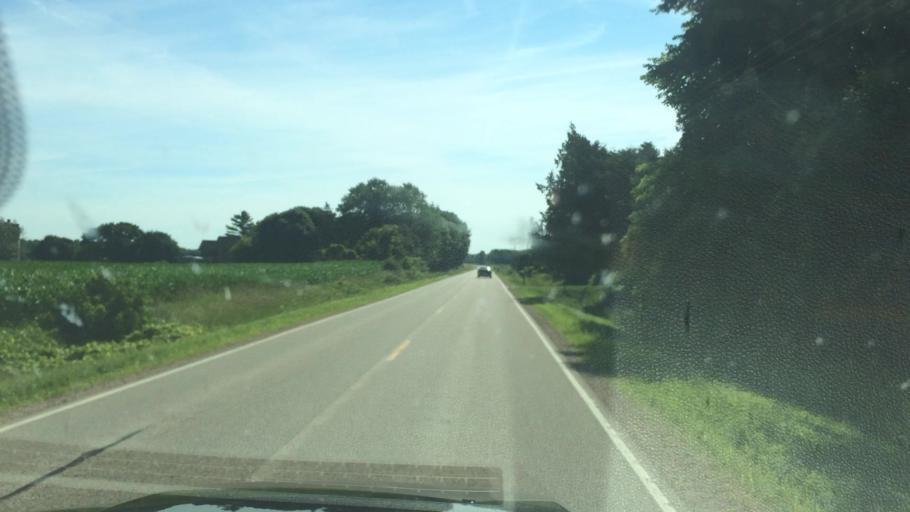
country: US
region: Wisconsin
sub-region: Oconto County
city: Gillett
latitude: 44.7875
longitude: -88.3240
